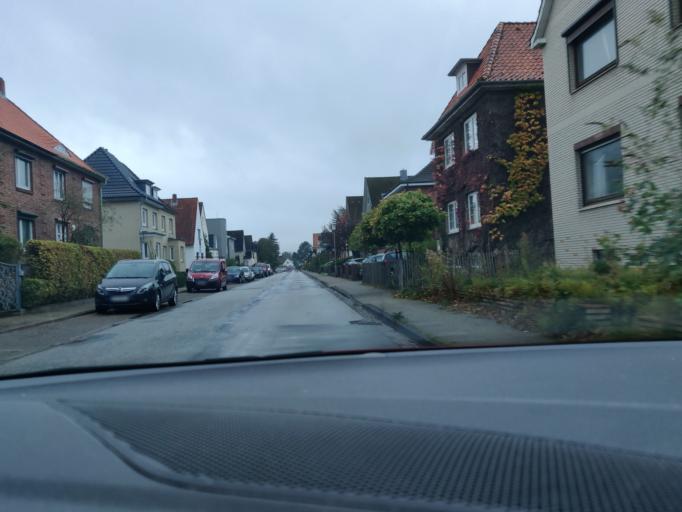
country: DE
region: Lower Saxony
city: Cuxhaven
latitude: 53.8767
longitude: 8.6846
